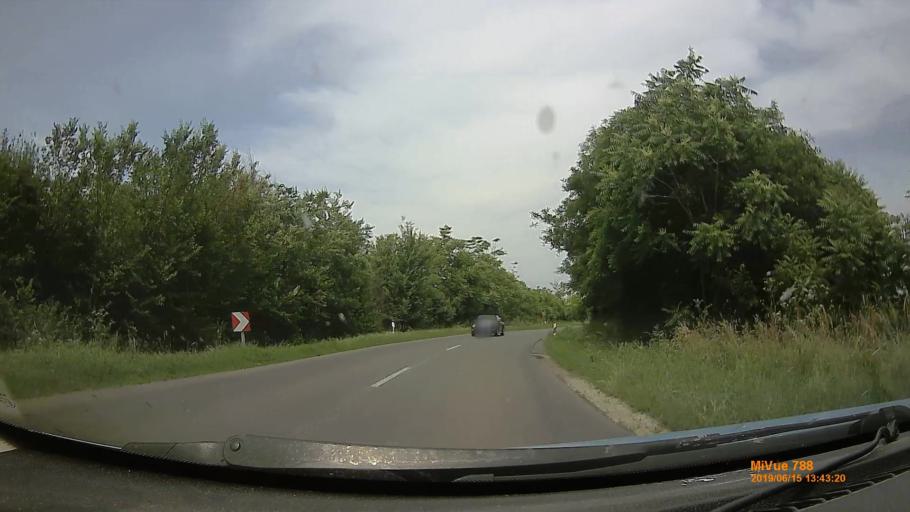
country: HU
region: Tolna
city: Iregszemcse
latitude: 46.6757
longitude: 18.1811
